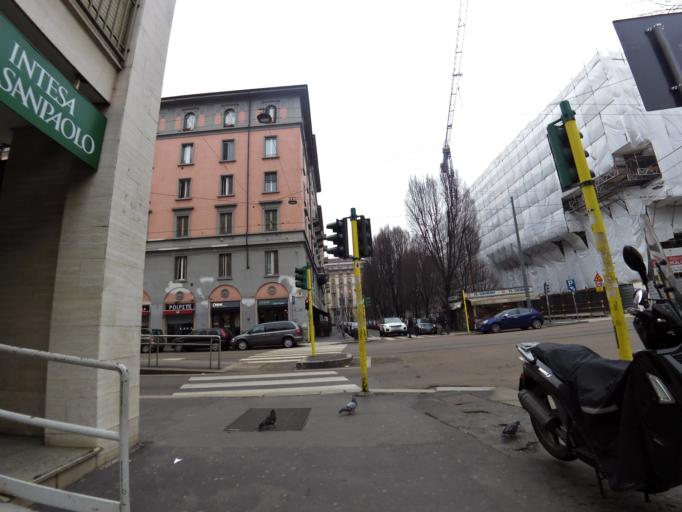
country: IT
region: Lombardy
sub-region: Citta metropolitana di Milano
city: Milano
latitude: 45.4507
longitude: 9.1939
